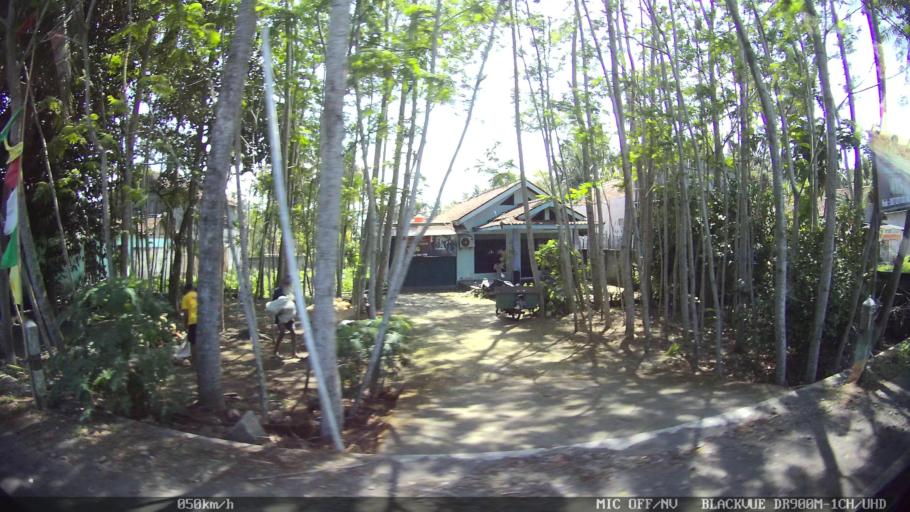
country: ID
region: Daerah Istimewa Yogyakarta
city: Srandakan
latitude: -7.9033
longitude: 110.0742
